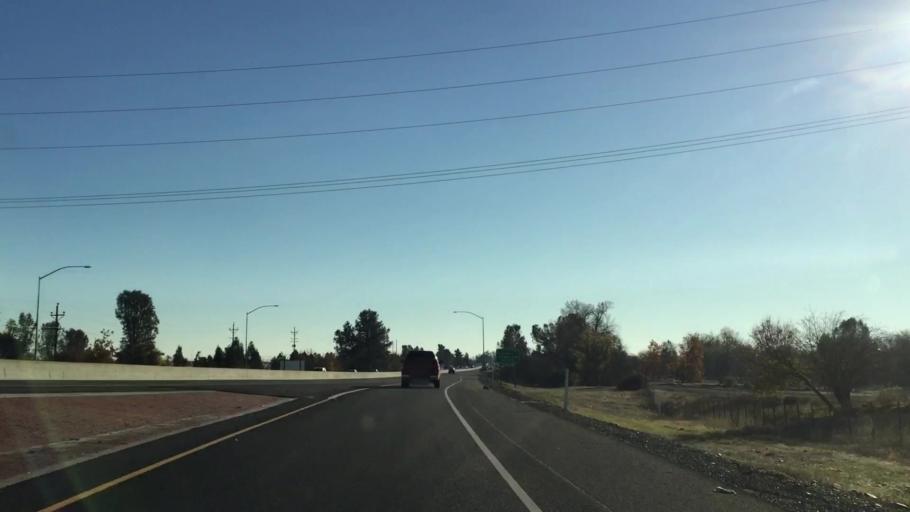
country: US
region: California
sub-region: Butte County
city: Thermalito
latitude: 39.5064
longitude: -121.5739
